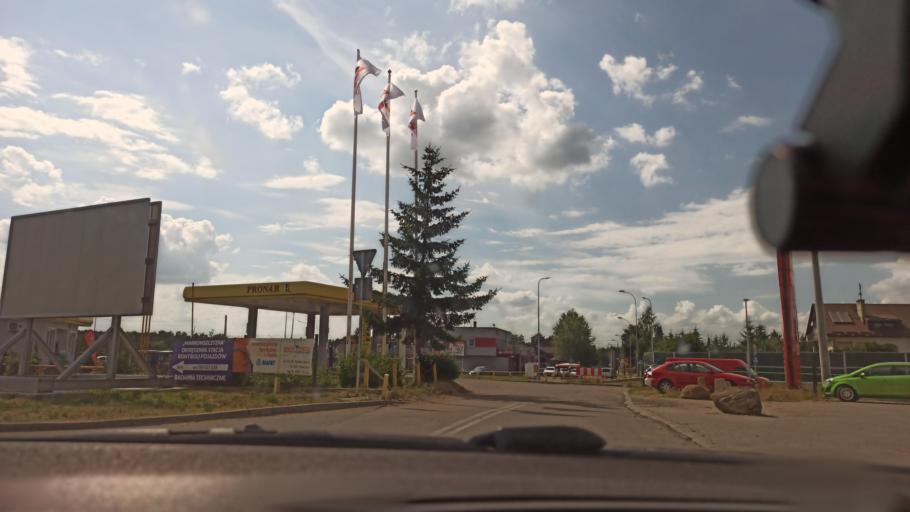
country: PL
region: Podlasie
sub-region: Powiat bialostocki
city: Turosn Koscielna
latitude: 53.0692
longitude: 23.0807
